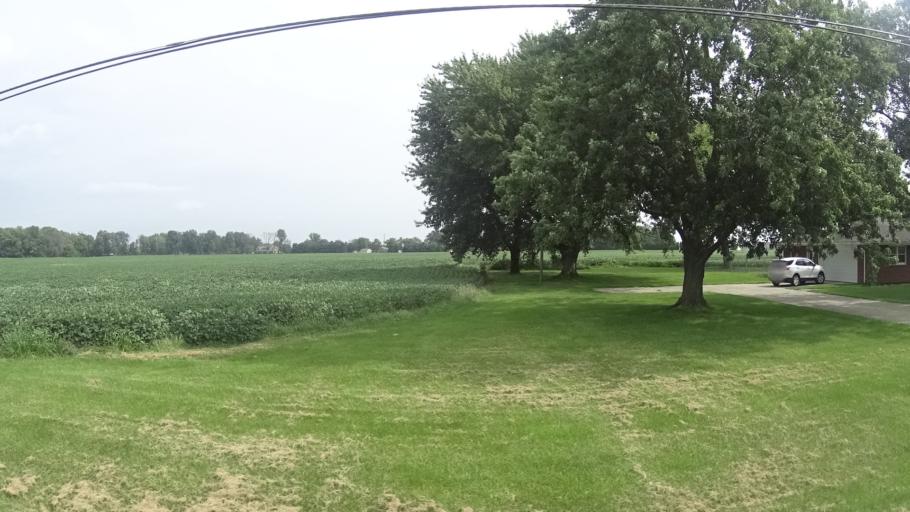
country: US
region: Indiana
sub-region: Madison County
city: Pendleton
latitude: 40.0130
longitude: -85.7581
